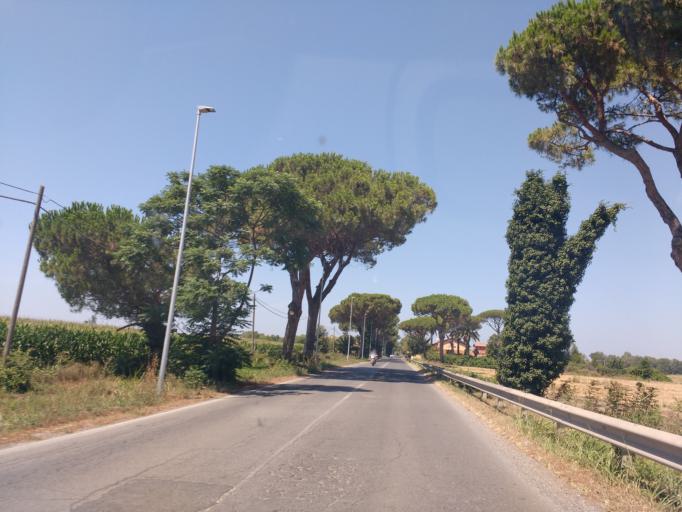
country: IT
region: Latium
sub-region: Citta metropolitana di Roma Capitale
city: Maccarese
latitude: 41.8781
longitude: 12.2093
